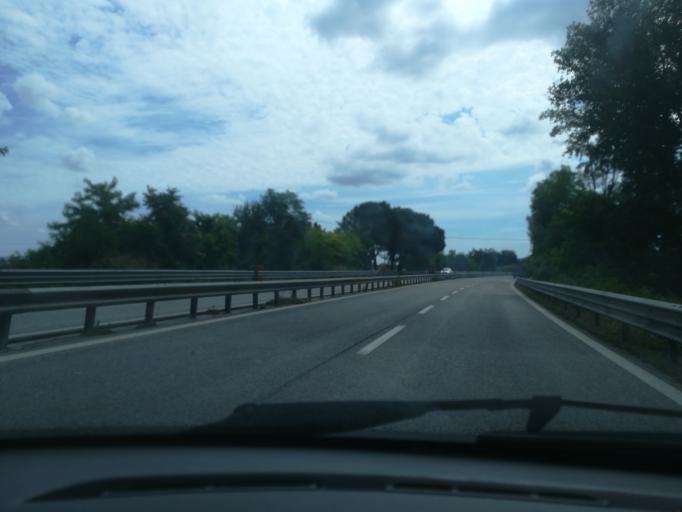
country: IT
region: The Marches
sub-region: Provincia di Macerata
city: Corridonia
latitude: 43.2656
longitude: 13.5432
